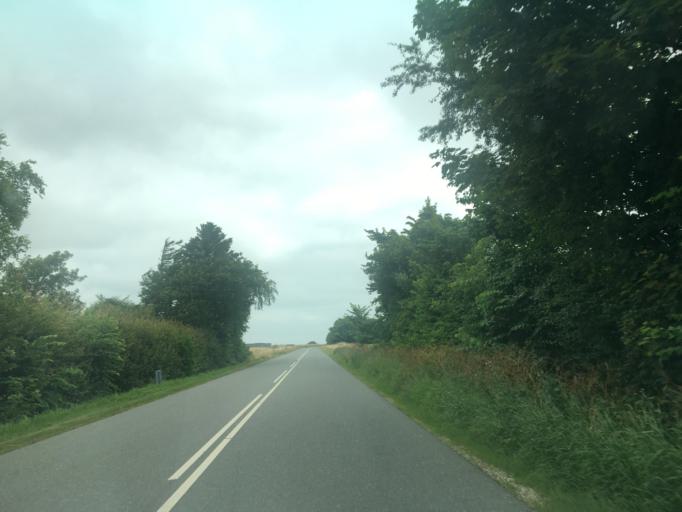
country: DK
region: North Denmark
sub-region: Thisted Kommune
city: Hurup
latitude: 56.8320
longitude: 8.5658
